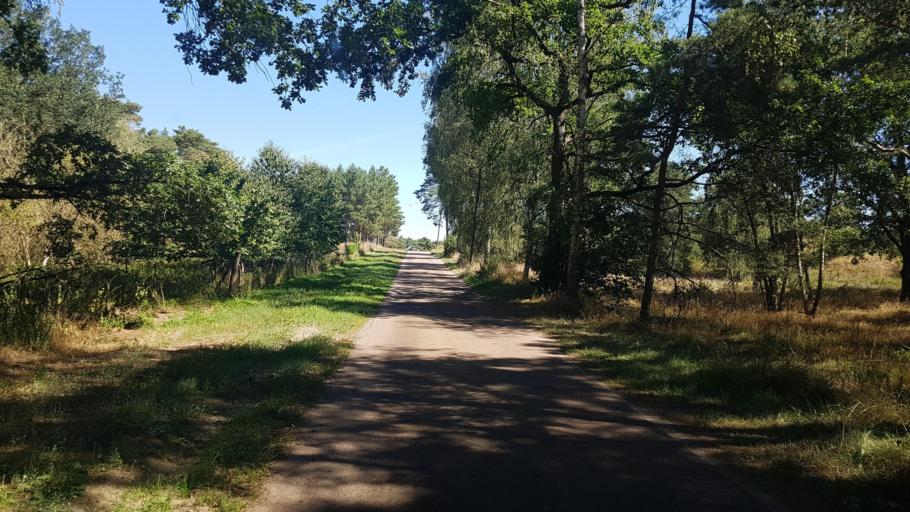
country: DE
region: Brandenburg
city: Golzow
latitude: 52.3012
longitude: 12.5800
